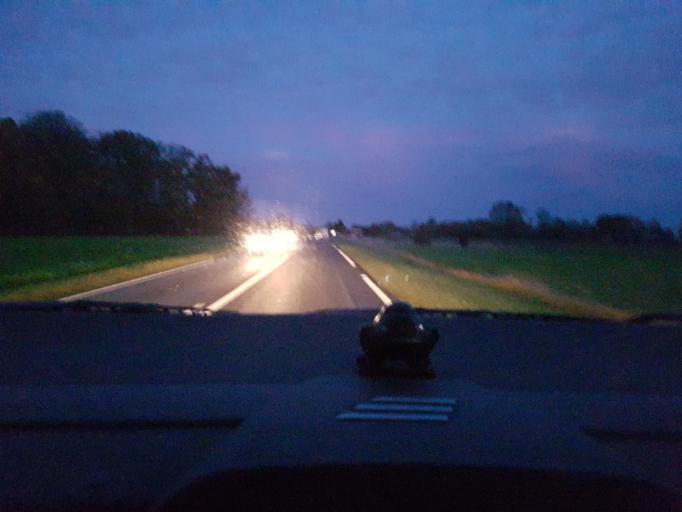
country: FR
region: Nord-Pas-de-Calais
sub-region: Departement du Pas-de-Calais
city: Beaumetz-les-Loges
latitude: 50.2358
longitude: 2.6469
